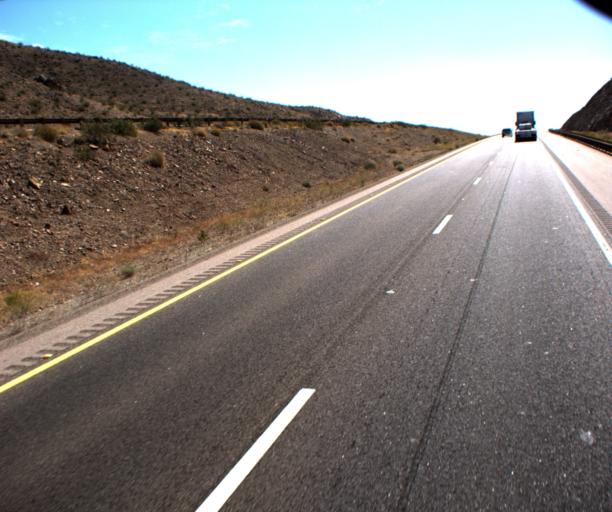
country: US
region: Nevada
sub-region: Clark County
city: Boulder City
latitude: 35.8479
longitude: -114.5856
